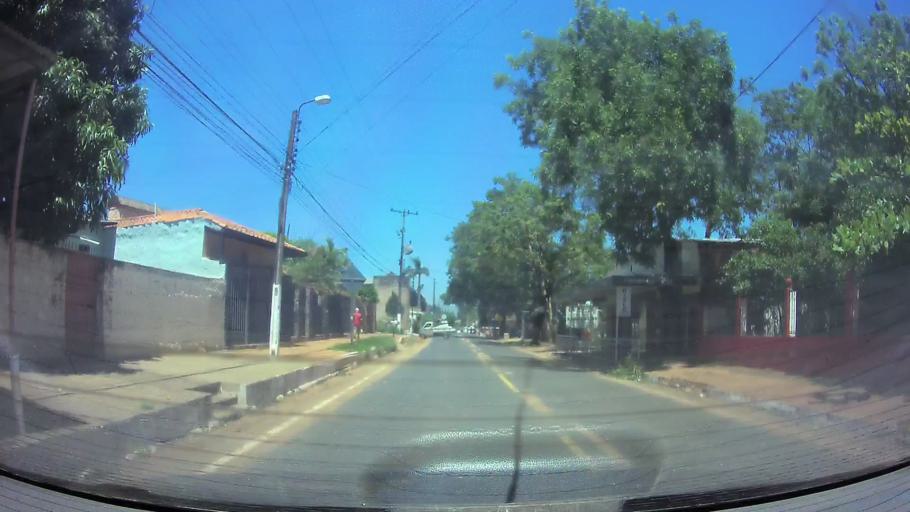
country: PY
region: Central
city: San Lorenzo
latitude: -25.3331
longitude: -57.4861
